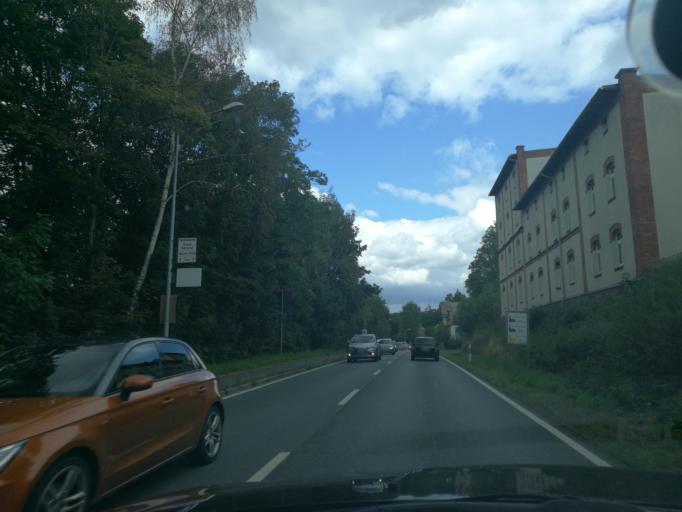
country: DE
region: Saxony
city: Oelsnitz
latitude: 50.4074
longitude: 12.1814
